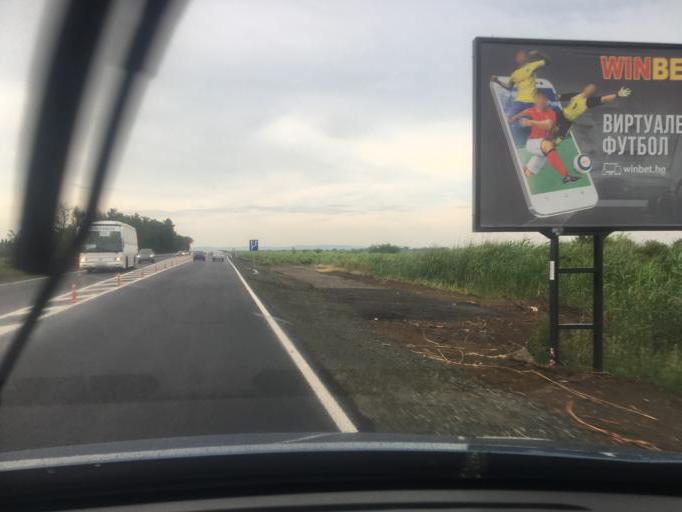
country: BG
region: Burgas
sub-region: Obshtina Pomorie
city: Pomorie
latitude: 42.5943
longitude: 27.6142
